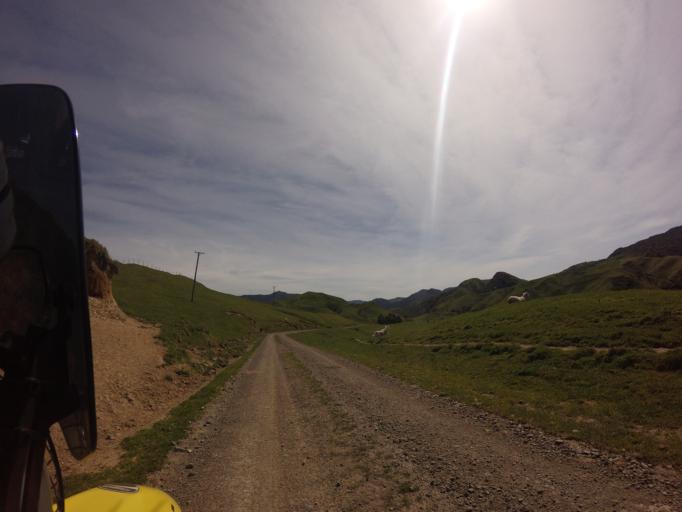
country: NZ
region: Bay of Plenty
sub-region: Opotiki District
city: Opotiki
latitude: -38.4561
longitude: 177.3723
